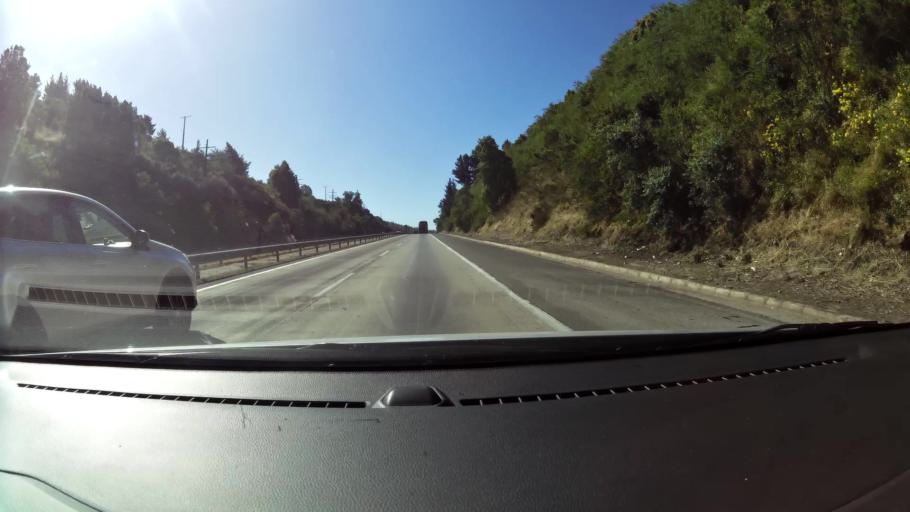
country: CL
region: Valparaiso
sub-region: Provincia de Marga Marga
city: Quilpue
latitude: -33.2351
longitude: -71.4611
